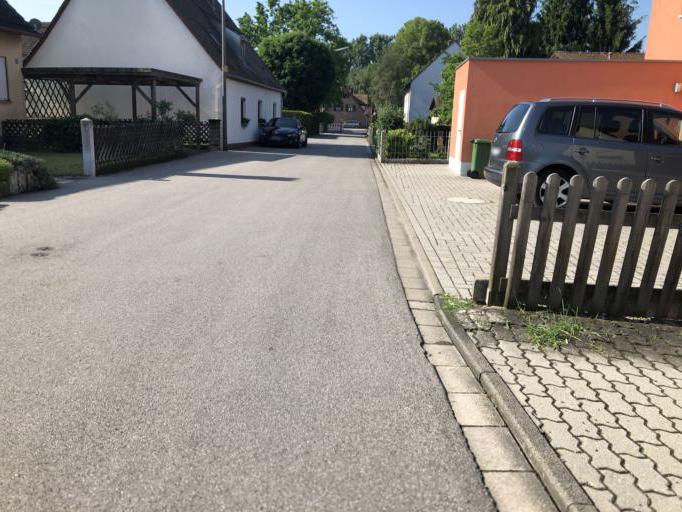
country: DE
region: Bavaria
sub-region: Regierungsbezirk Mittelfranken
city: Erlangen
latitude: 49.5506
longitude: 11.0261
